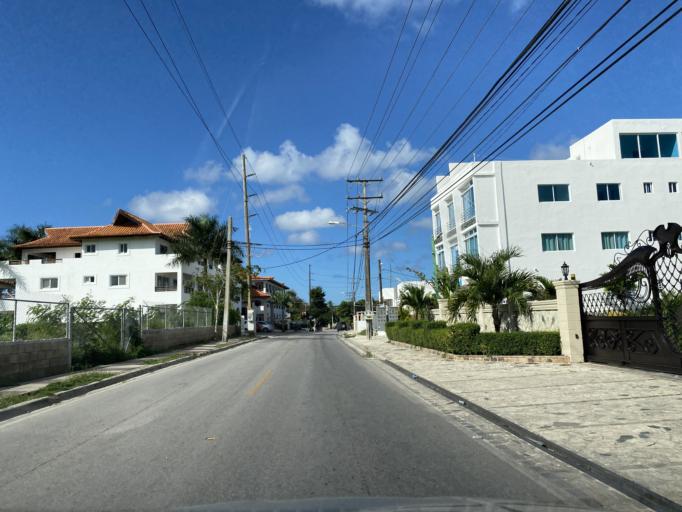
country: DO
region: La Romana
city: La Romana
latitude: 18.3702
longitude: -68.8364
